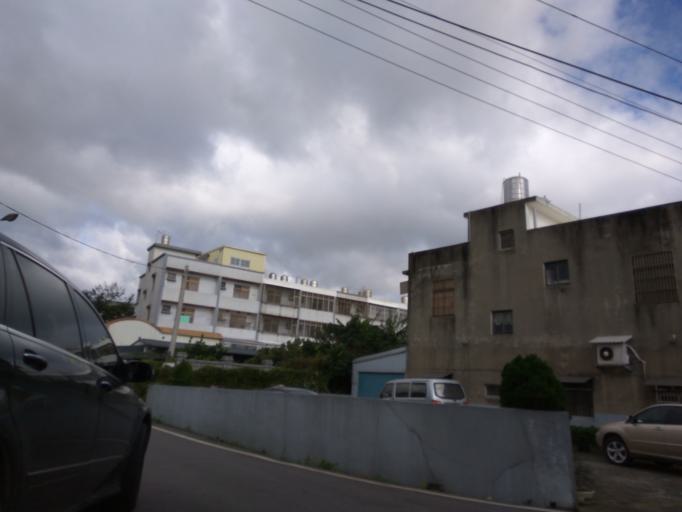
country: TW
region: Taiwan
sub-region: Hsinchu
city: Zhubei
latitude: 24.9736
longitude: 121.0818
